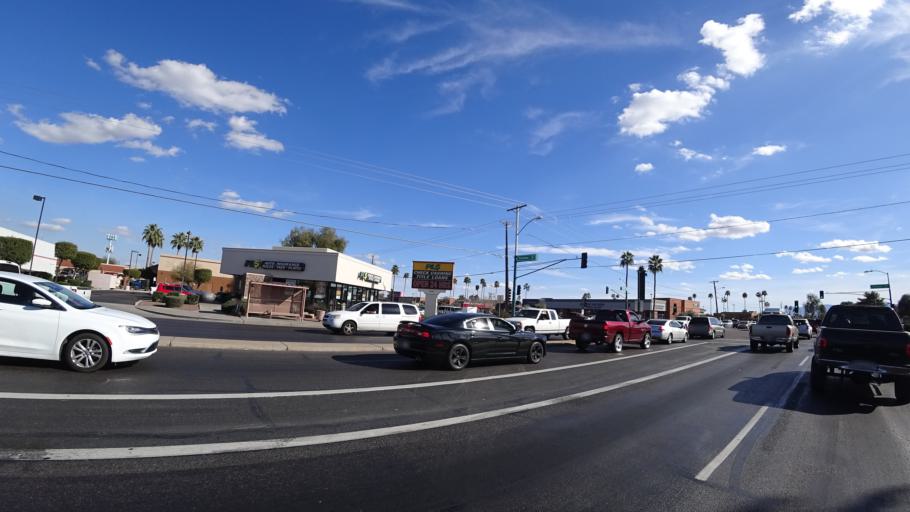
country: US
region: Arizona
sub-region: Maricopa County
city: Tolleson
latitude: 33.4807
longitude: -112.2207
